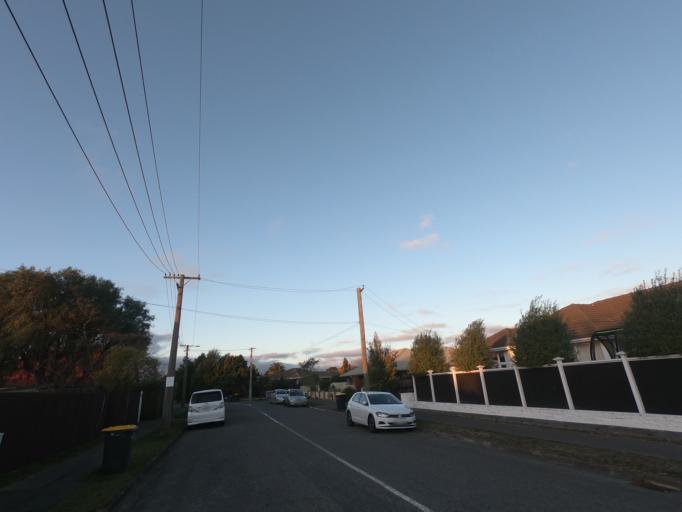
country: NZ
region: Canterbury
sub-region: Selwyn District
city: Prebbleton
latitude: -43.5762
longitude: 172.5596
